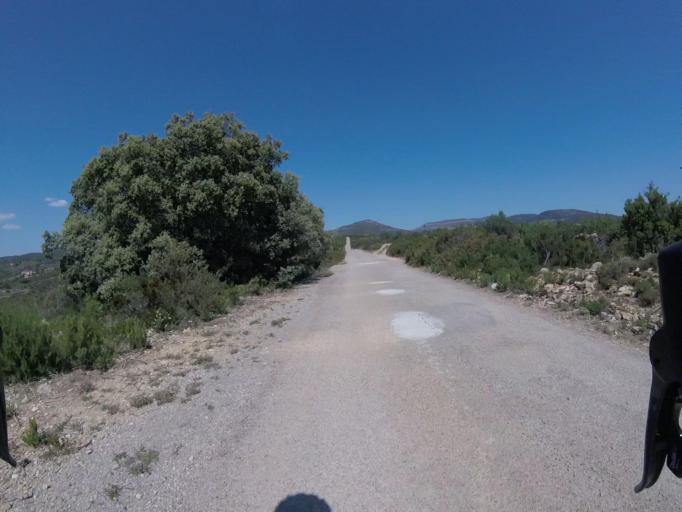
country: ES
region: Valencia
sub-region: Provincia de Castello
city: Sierra-Engarceran
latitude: 40.2292
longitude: -0.0239
